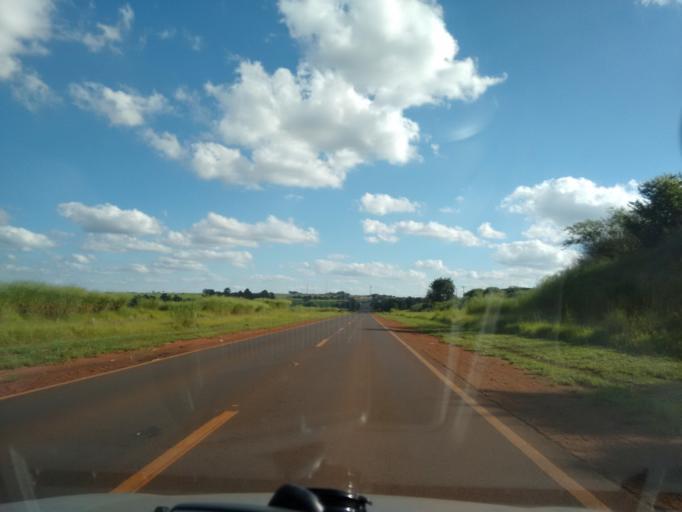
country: BR
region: Sao Paulo
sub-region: Americo Brasiliense
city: Americo Brasiliense
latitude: -21.6777
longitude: -48.0704
